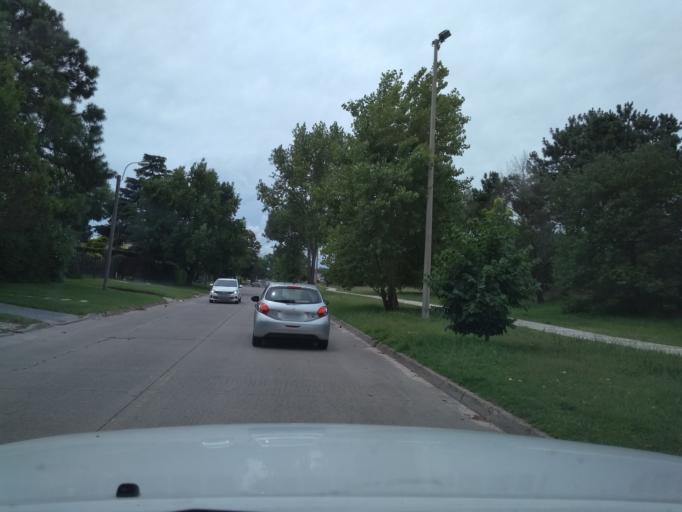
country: UY
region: Canelones
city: Paso de Carrasco
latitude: -34.8753
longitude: -56.0581
